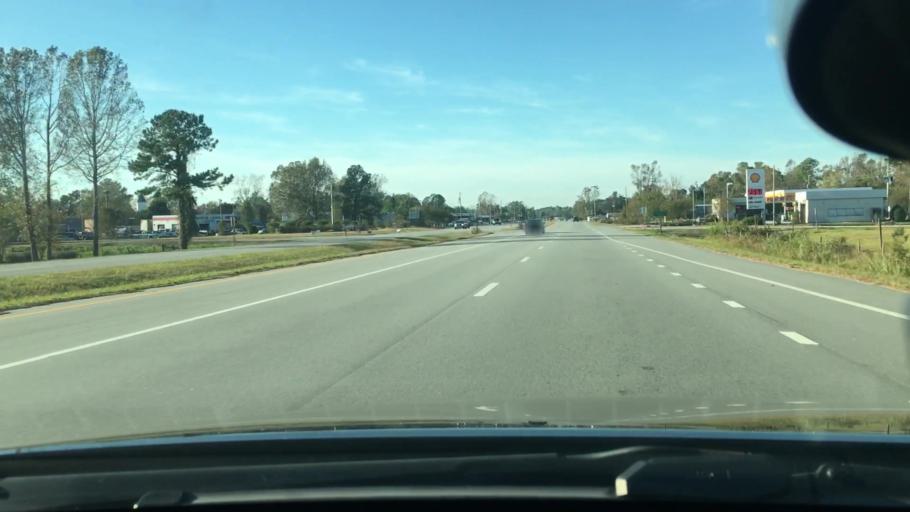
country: US
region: North Carolina
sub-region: Craven County
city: New Bern
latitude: 35.1189
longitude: -77.0164
